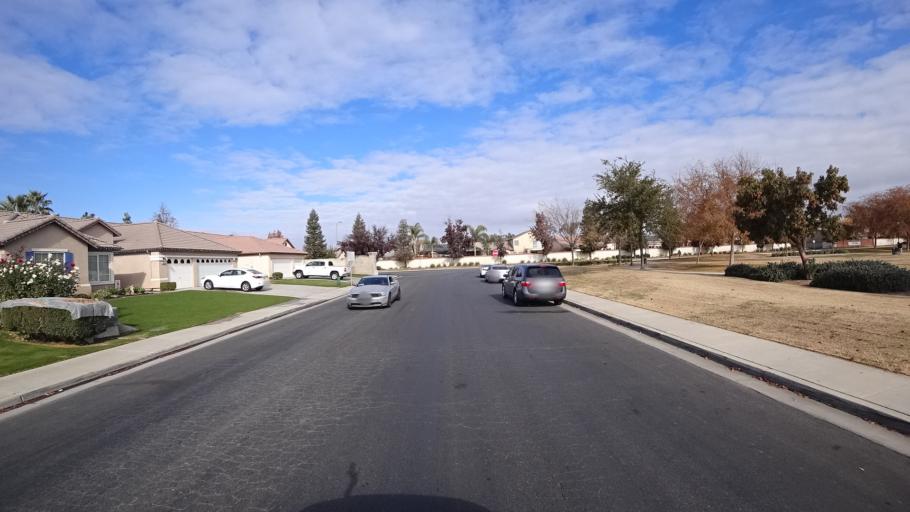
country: US
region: California
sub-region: Kern County
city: Greenacres
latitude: 35.3029
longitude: -119.1219
